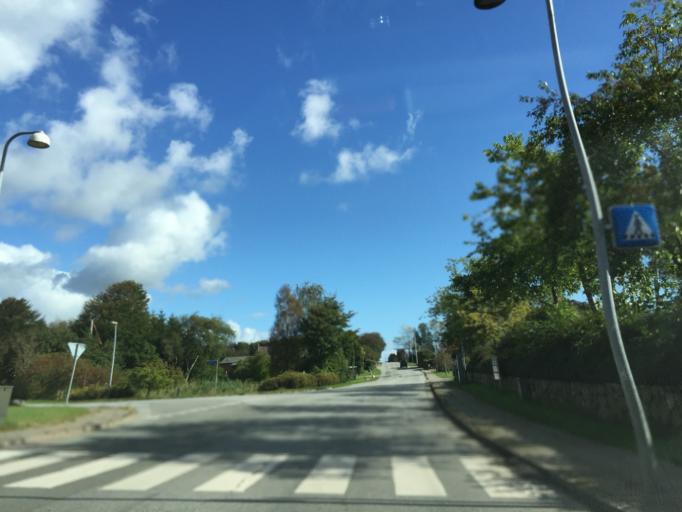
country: DK
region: Central Jutland
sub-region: Viborg Kommune
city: Viborg
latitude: 56.4416
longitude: 9.4870
